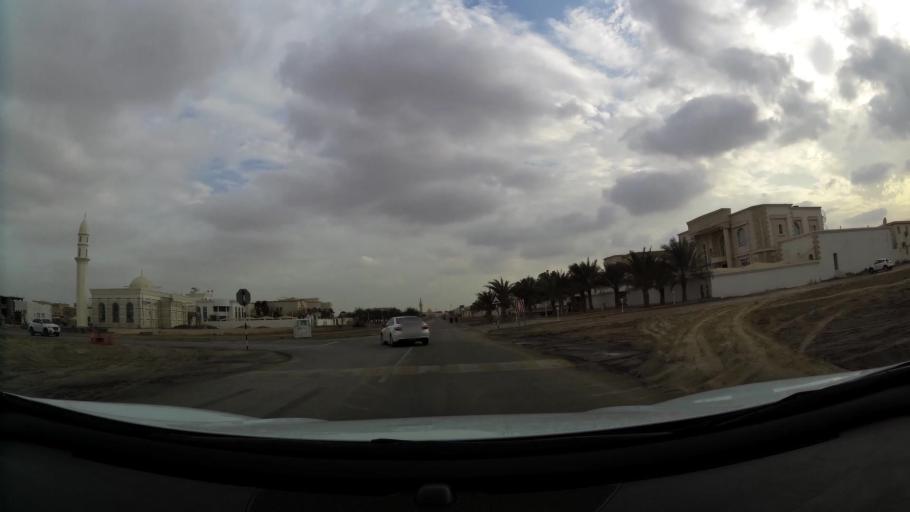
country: AE
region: Abu Dhabi
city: Abu Dhabi
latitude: 24.3604
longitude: 54.5454
